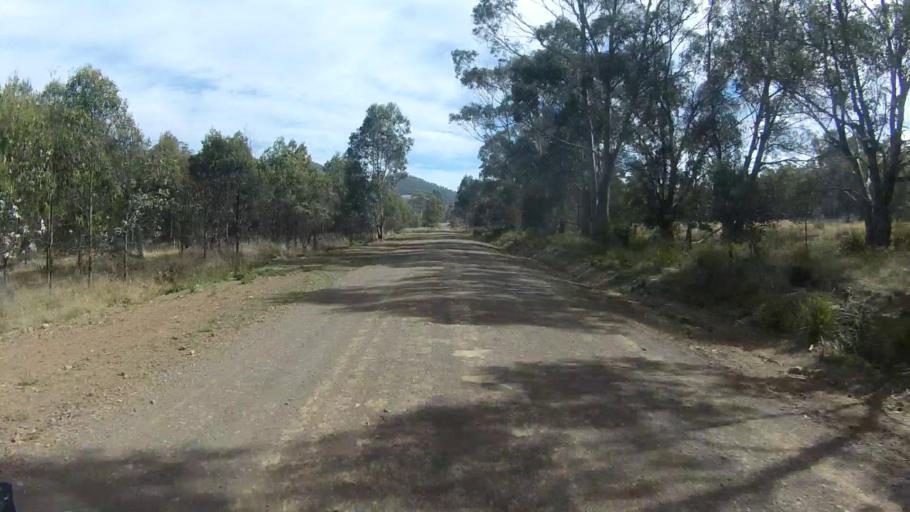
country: AU
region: Tasmania
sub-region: Sorell
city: Sorell
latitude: -42.6554
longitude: 147.8981
